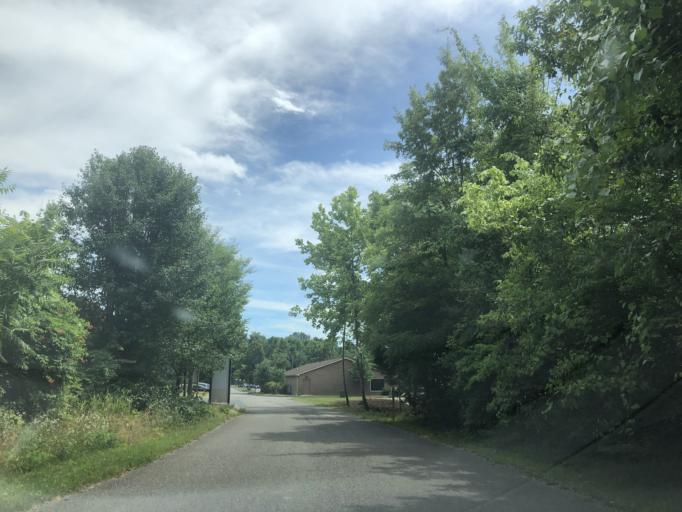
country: US
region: Tennessee
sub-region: Davidson County
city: Belle Meade
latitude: 36.0784
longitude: -86.9438
